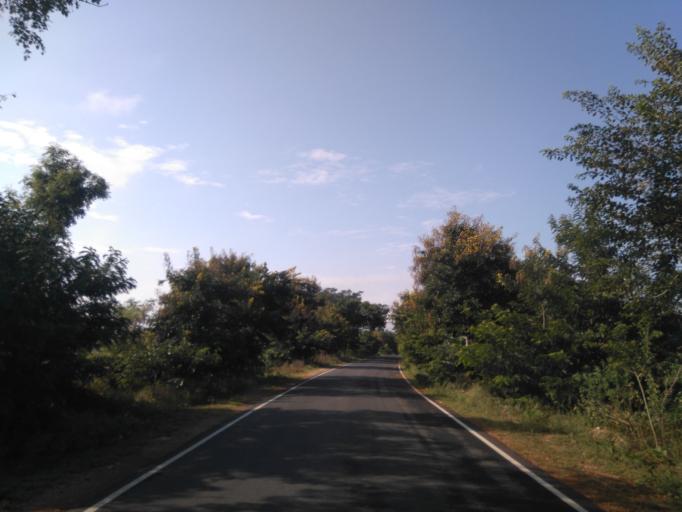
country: IN
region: Karnataka
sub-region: Mandya
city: Malavalli
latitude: 12.3028
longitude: 77.0725
